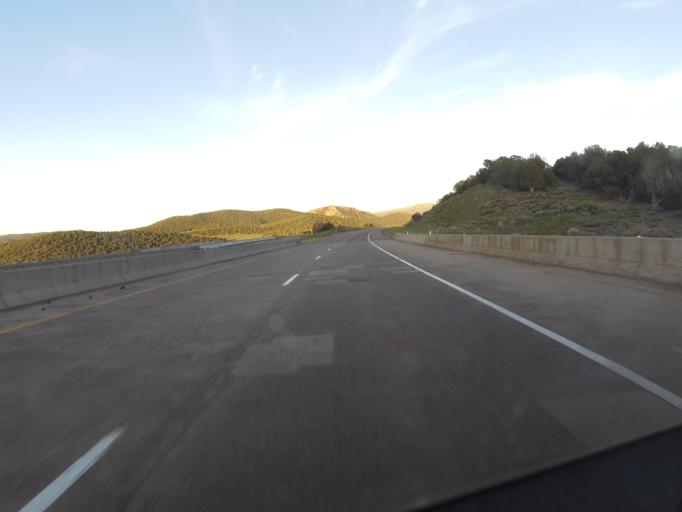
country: US
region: Utah
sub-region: Sevier County
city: Monroe
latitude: 38.5732
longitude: -112.4598
